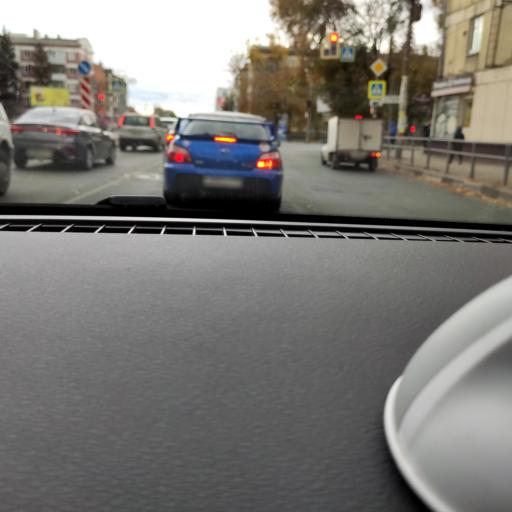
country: RU
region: Samara
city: Samara
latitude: 53.2011
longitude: 50.1900
